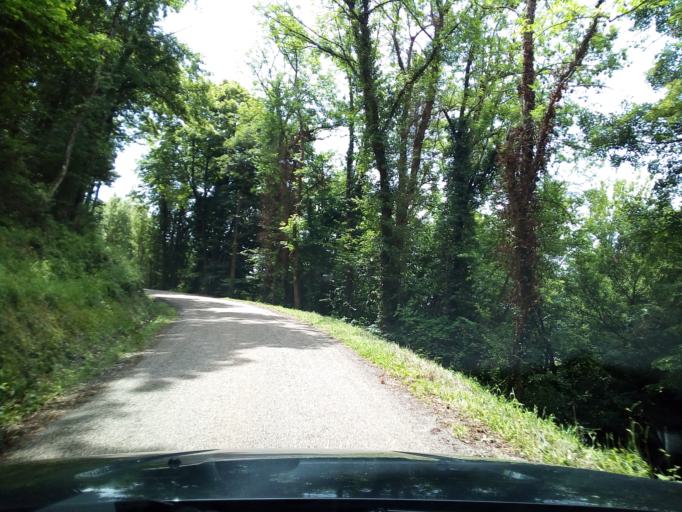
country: FR
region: Rhone-Alpes
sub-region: Departement de l'Isere
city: Poisat
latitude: 45.1569
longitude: 5.7758
